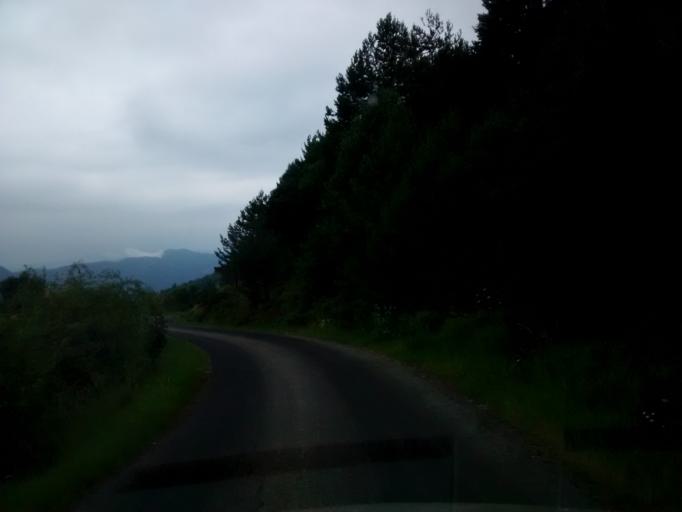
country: ES
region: Aragon
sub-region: Provincia de Huesca
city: Puertolas
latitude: 42.5593
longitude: 0.1417
